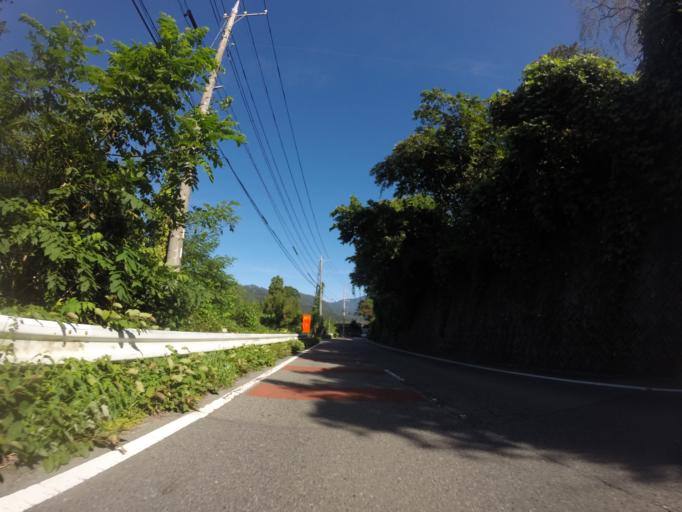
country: JP
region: Shizuoka
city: Fujinomiya
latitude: 35.3193
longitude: 138.4529
